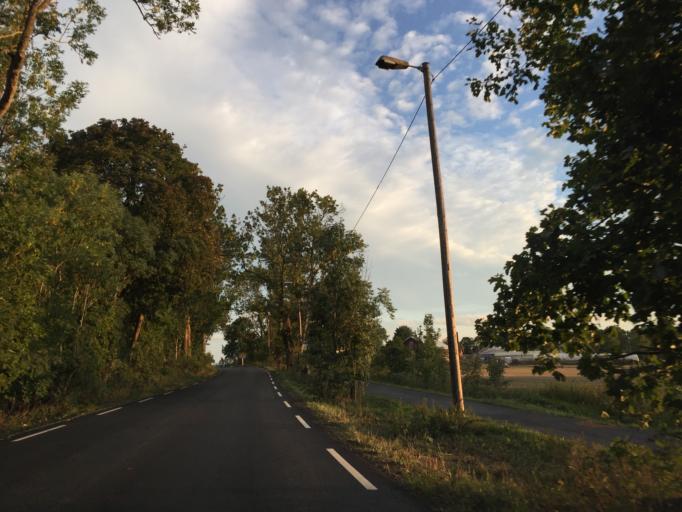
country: NO
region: Akershus
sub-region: As
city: As
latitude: 59.7087
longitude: 10.7718
